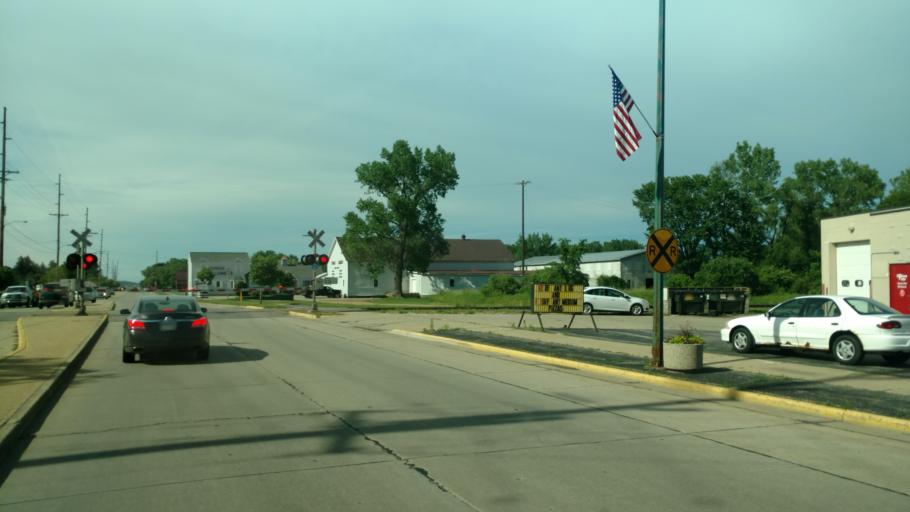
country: US
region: Wisconsin
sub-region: Monroe County
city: Tomah
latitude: 43.9855
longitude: -90.5046
